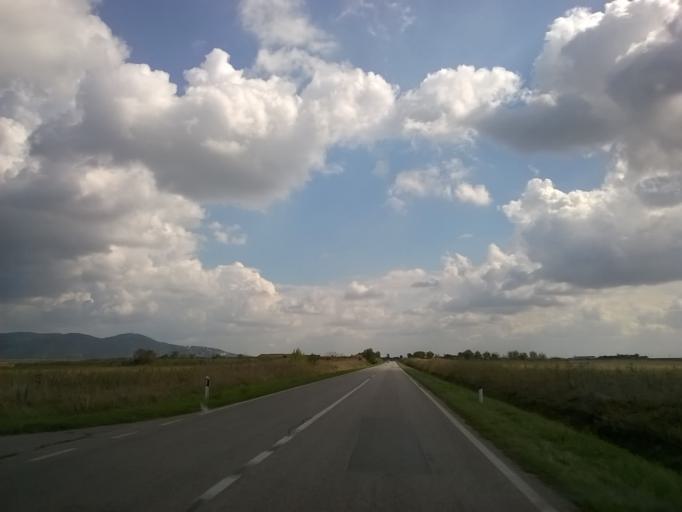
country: RS
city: Pavlis
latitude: 45.1509
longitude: 21.2572
